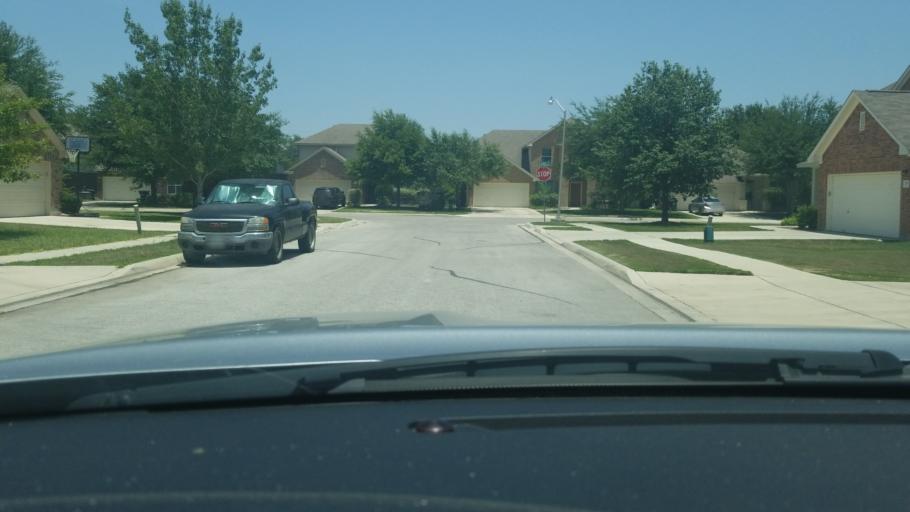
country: US
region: Texas
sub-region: Guadalupe County
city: Cibolo
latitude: 29.5763
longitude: -98.2270
